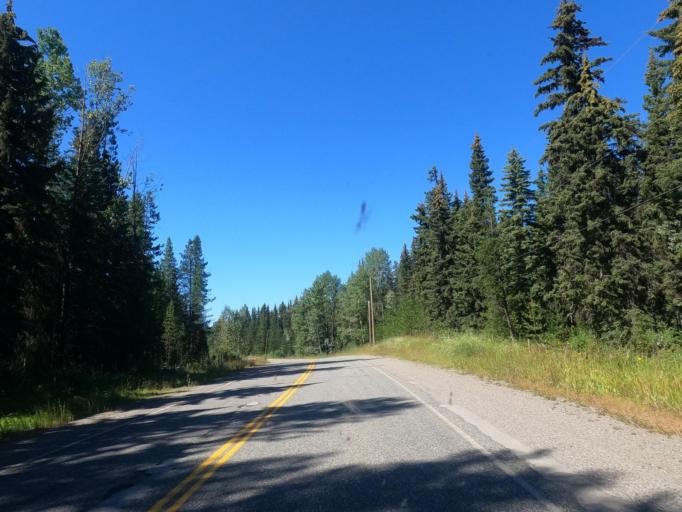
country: CA
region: British Columbia
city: Quesnel
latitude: 53.0428
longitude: -122.2546
